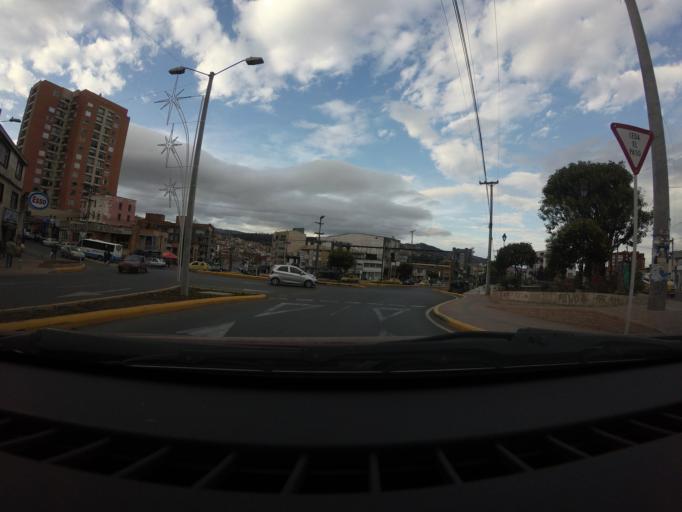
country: CO
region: Boyaca
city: Tunja
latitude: 5.5431
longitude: -73.3586
